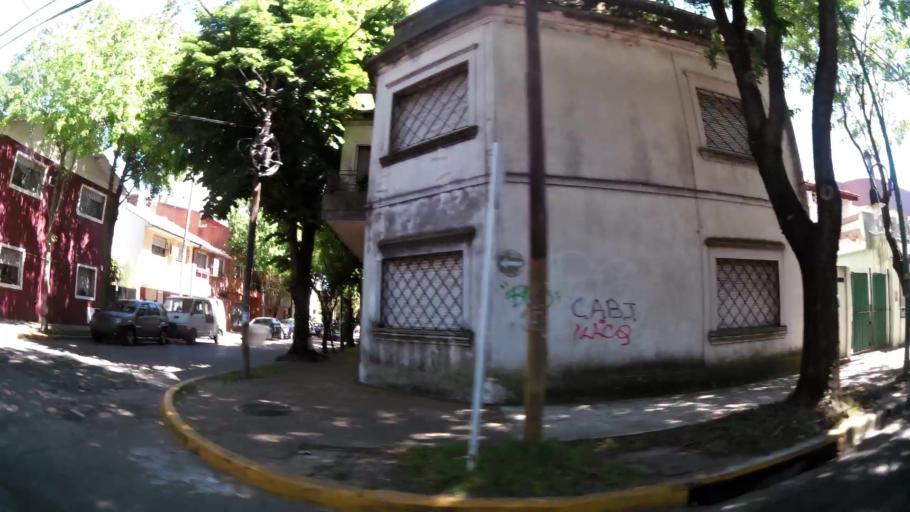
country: AR
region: Buenos Aires
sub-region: Partido de Vicente Lopez
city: Olivos
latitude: -34.5028
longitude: -58.4932
